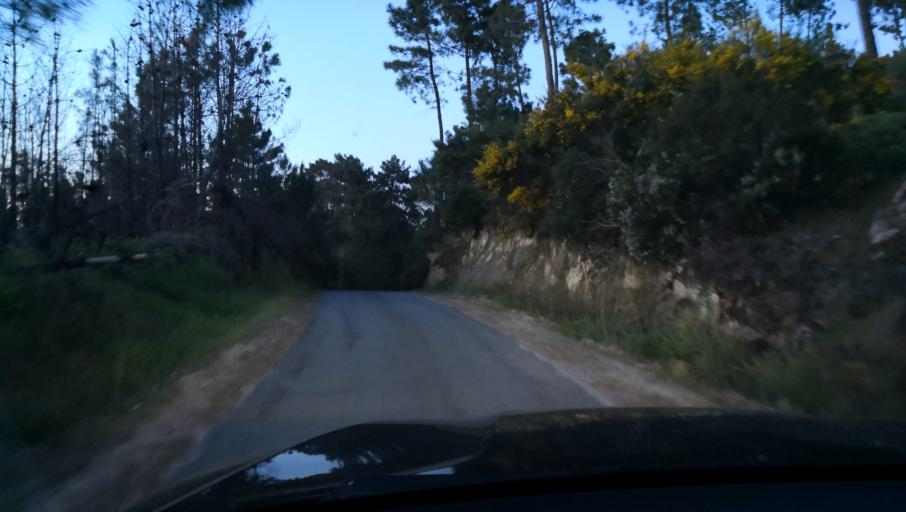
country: PT
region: Vila Real
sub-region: Vila Real
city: Vila Real
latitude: 41.3060
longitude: -7.6849
